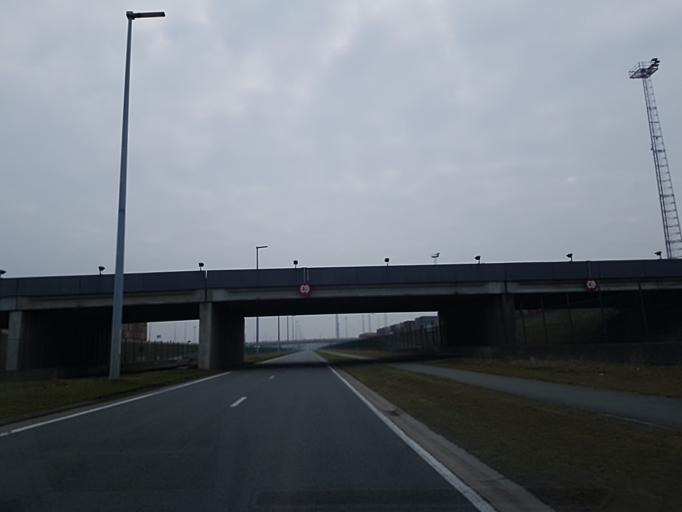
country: BE
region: Flanders
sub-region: Provincie Oost-Vlaanderen
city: Beveren
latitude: 51.2927
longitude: 4.2492
